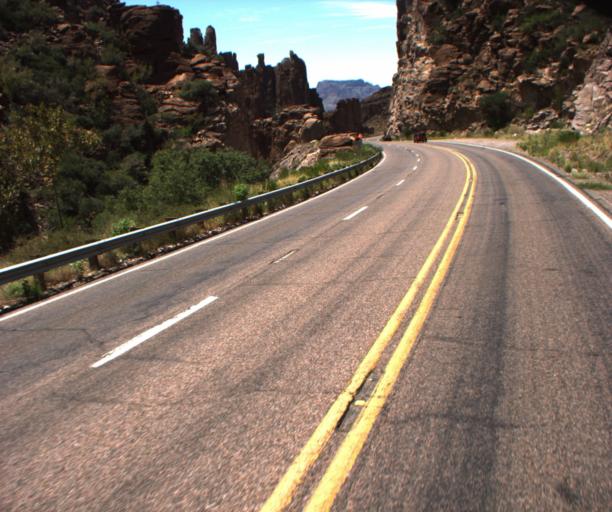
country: US
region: Arizona
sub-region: Pinal County
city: Superior
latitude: 33.3084
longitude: -111.0716
